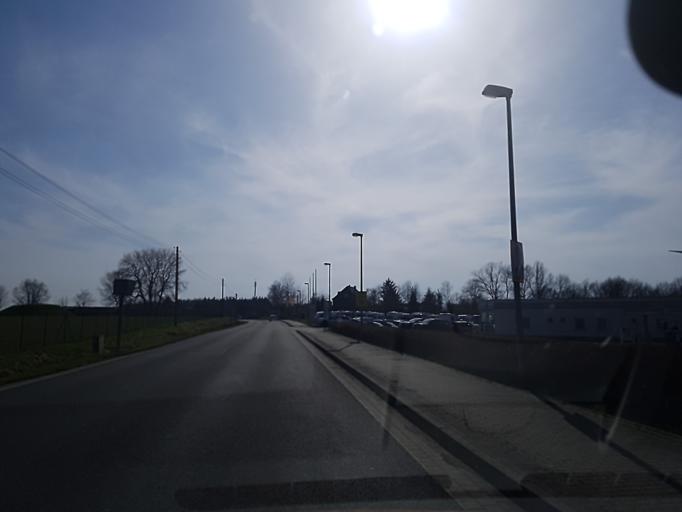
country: DE
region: Brandenburg
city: Calau
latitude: 51.7435
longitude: 13.9419
